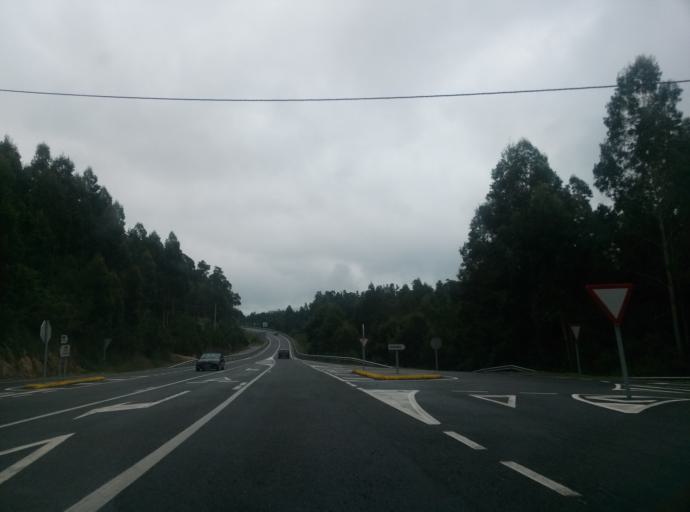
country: ES
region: Galicia
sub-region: Provincia de Lugo
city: Viveiro
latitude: 43.5722
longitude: -7.6368
